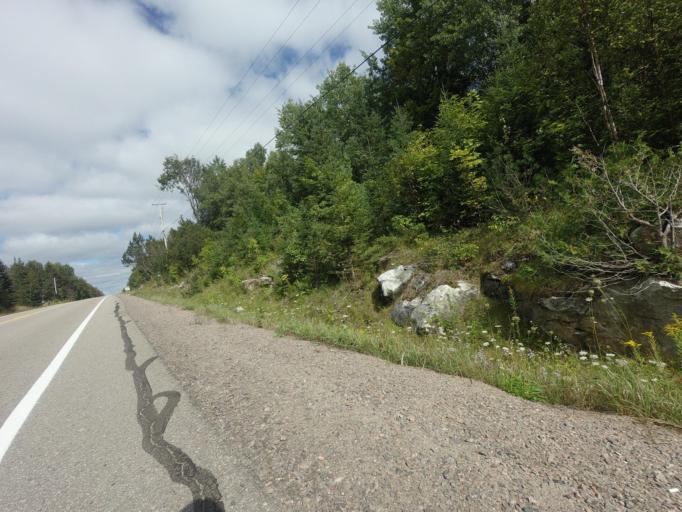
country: CA
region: Ontario
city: Bancroft
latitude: 44.9608
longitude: -78.2855
